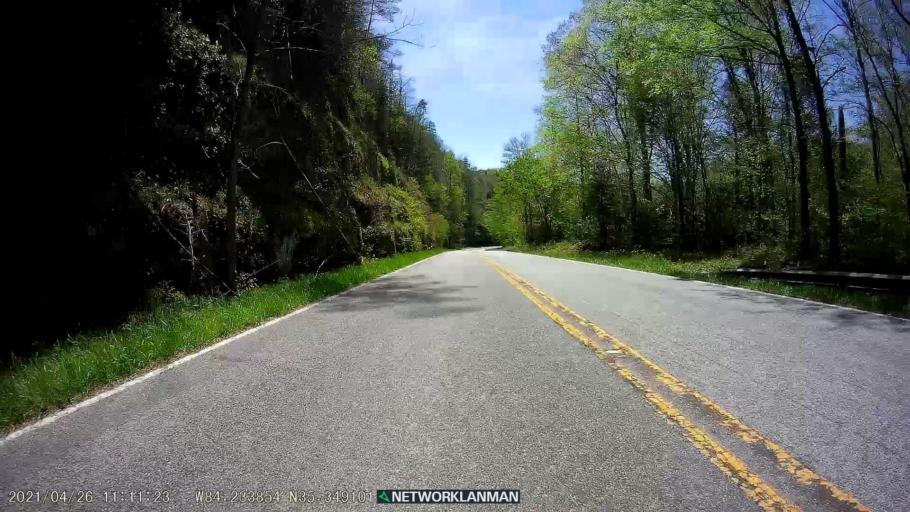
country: US
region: Tennessee
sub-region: Monroe County
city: Madisonville
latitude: 35.3492
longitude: -84.2338
